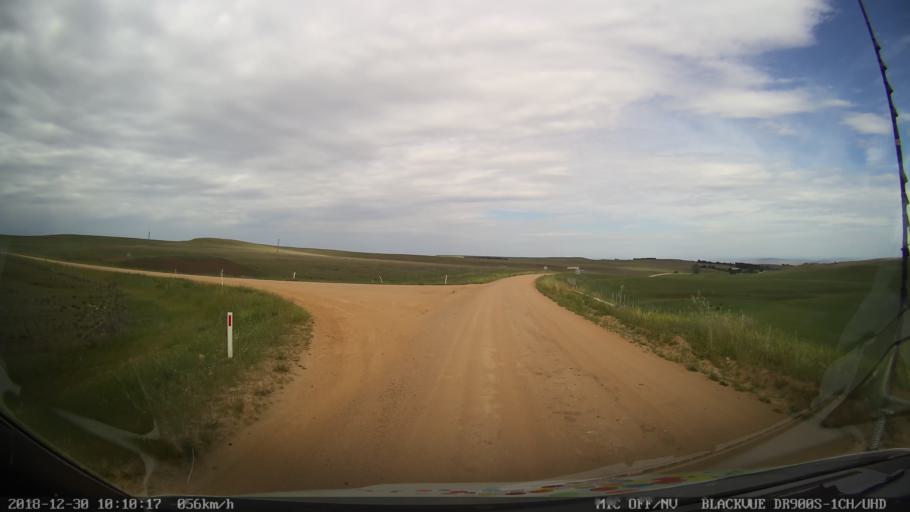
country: AU
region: New South Wales
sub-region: Cooma-Monaro
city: Cooma
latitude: -36.5508
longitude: 149.0965
